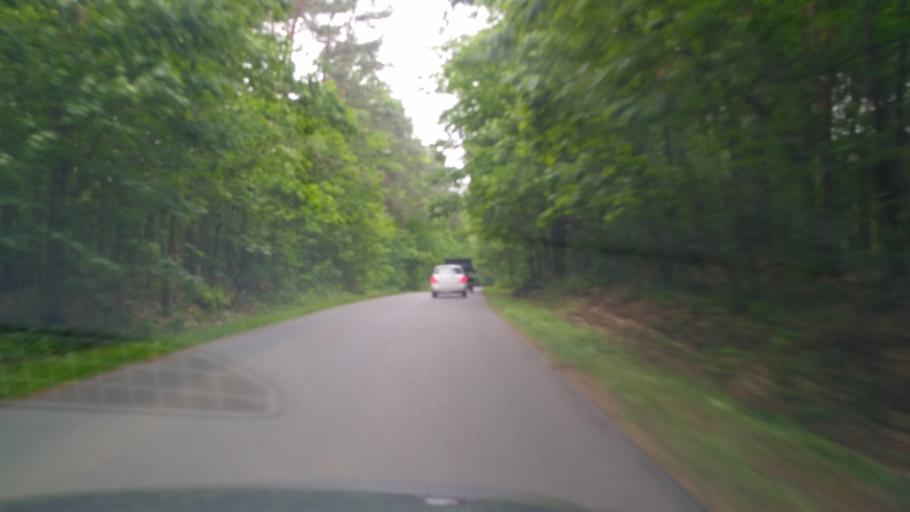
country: PL
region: Subcarpathian Voivodeship
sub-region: Powiat kolbuszowski
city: Niwiska
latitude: 50.1760
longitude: 21.6635
